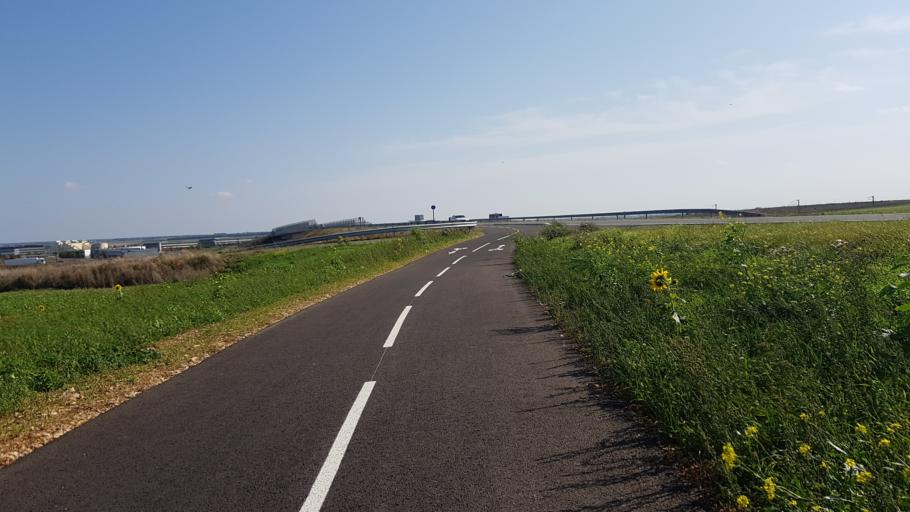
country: FR
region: Poitou-Charentes
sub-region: Departement de la Vienne
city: Chasseneuil-du-Poitou
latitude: 46.6572
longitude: 0.3502
